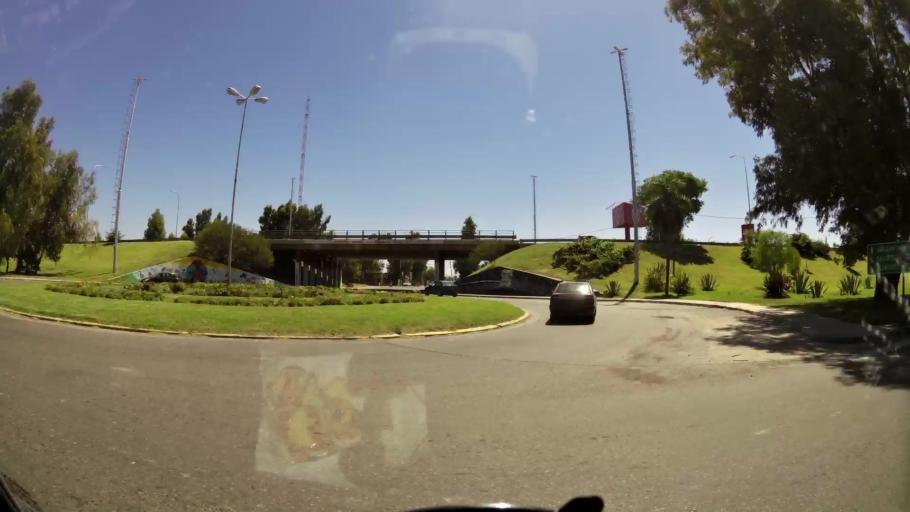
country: AR
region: San Juan
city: San Juan
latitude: -31.5234
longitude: -68.5421
